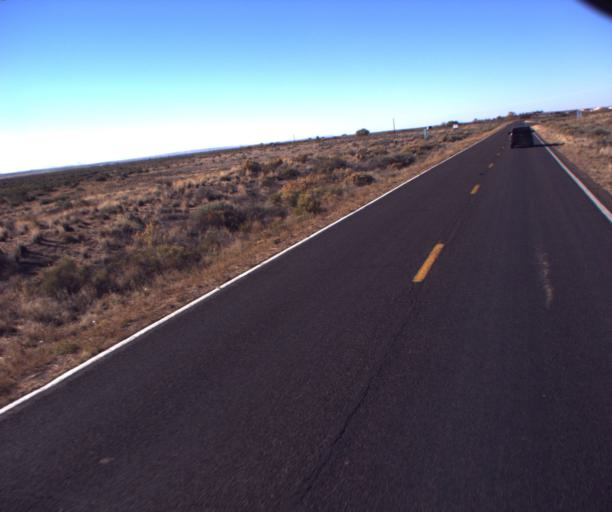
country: US
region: Arizona
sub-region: Navajo County
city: First Mesa
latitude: 35.8093
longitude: -110.4145
